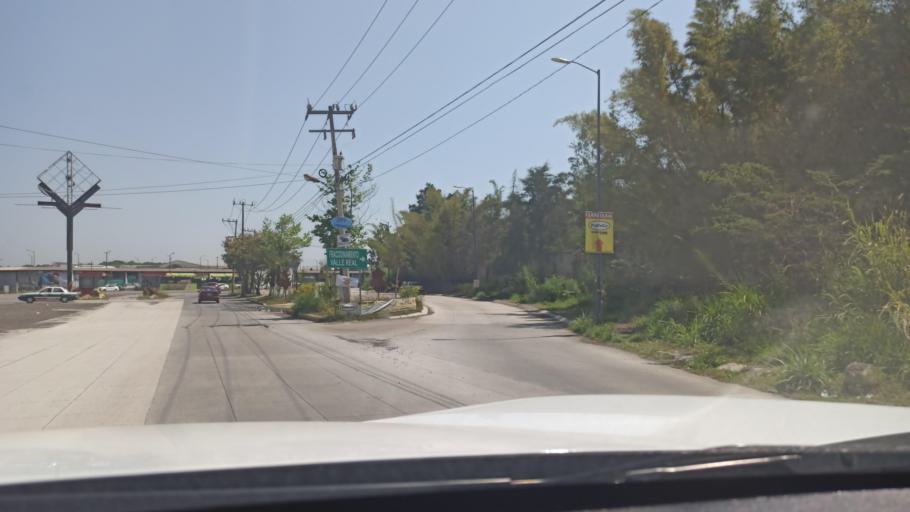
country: MX
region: Veracruz
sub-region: Emiliano Zapata
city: Las Trancas
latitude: 19.5137
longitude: -96.8550
